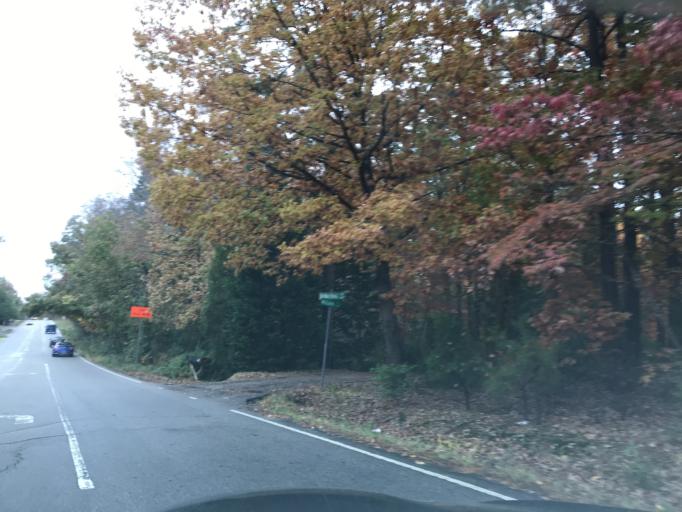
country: US
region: North Carolina
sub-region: Wake County
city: Raleigh
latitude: 35.8438
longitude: -78.6098
